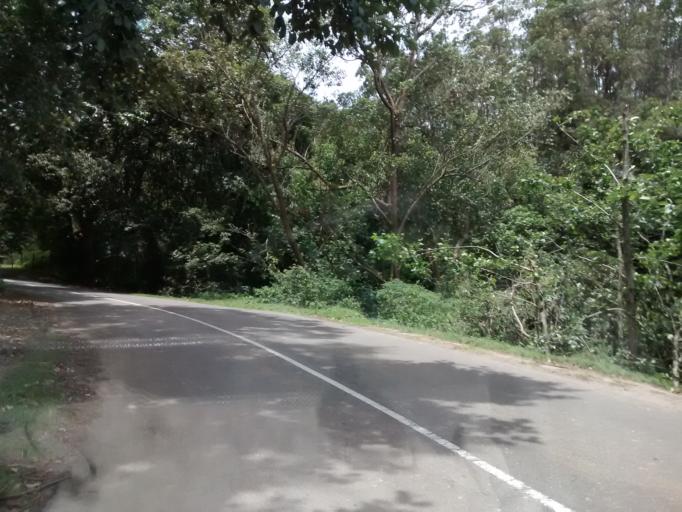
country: IN
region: Kerala
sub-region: Idukki
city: Munnar
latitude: 10.1380
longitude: 77.2027
